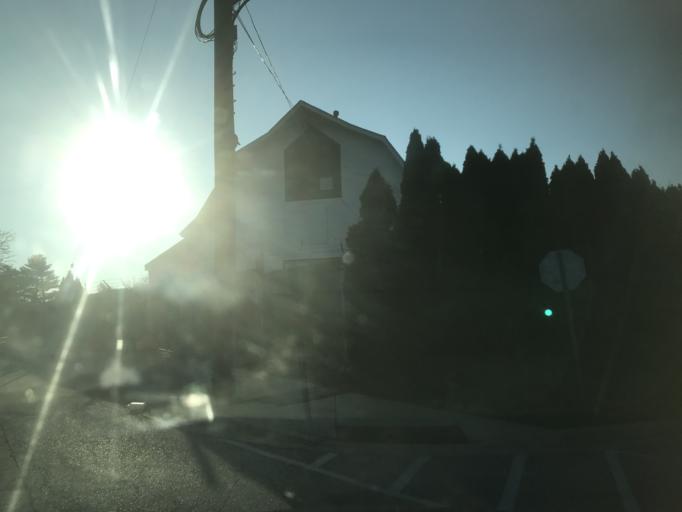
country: US
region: Maryland
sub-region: Baltimore County
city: Towson
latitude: 39.3911
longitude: -76.5776
